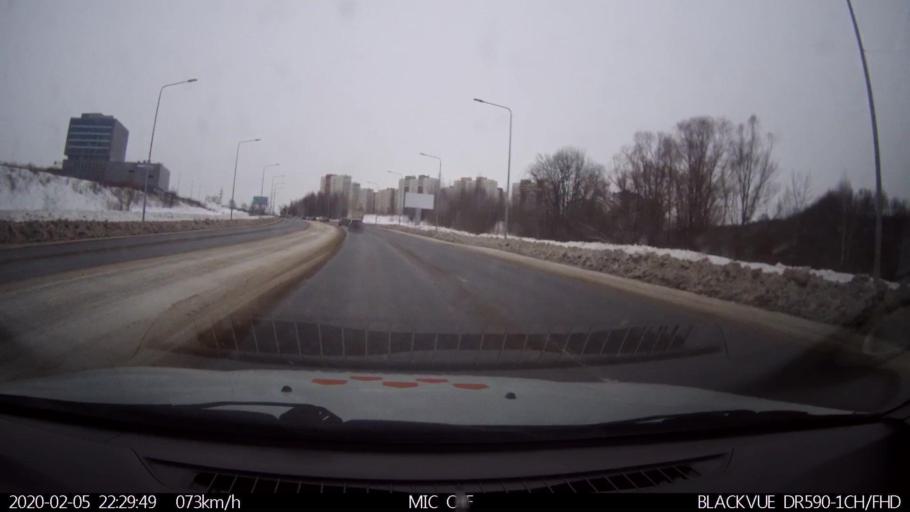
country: RU
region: Nizjnij Novgorod
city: Imeni Stepana Razina
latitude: 54.7466
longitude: 44.1494
